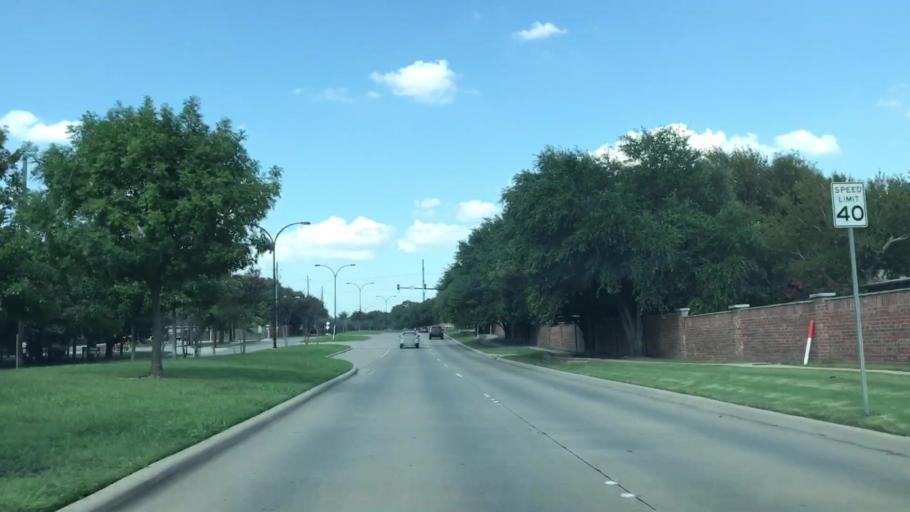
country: US
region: Texas
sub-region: Tarrant County
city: Keller
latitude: 32.9064
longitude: -97.2343
